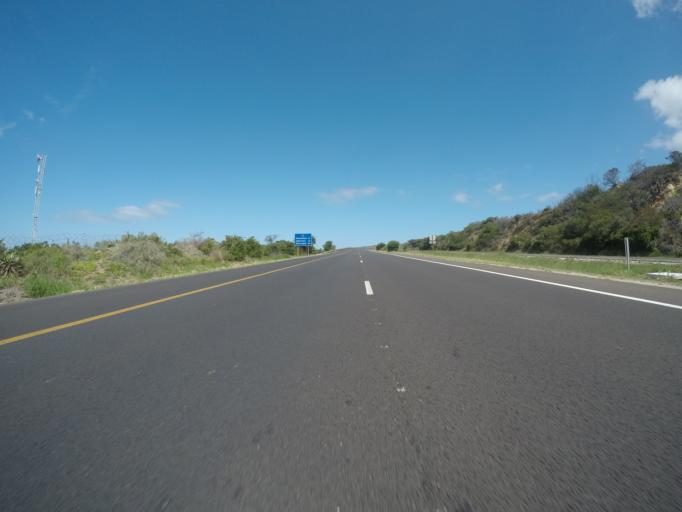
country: ZA
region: Western Cape
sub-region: Eden District Municipality
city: Mossel Bay
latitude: -34.1554
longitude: 22.0995
